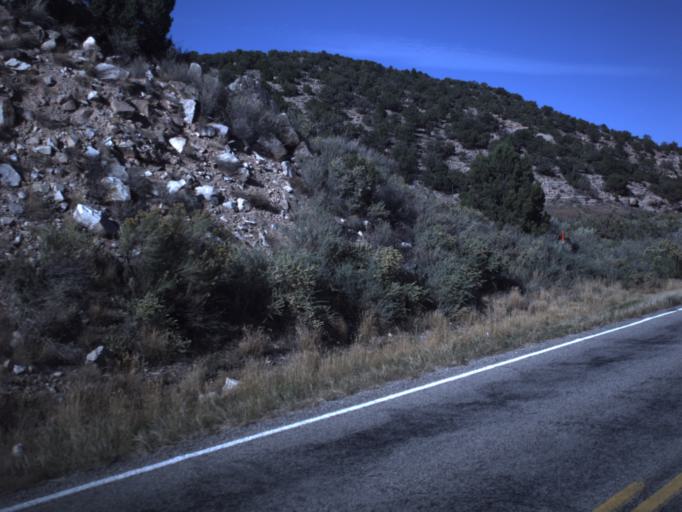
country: US
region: Utah
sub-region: Grand County
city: Moab
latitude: 38.3058
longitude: -109.3641
